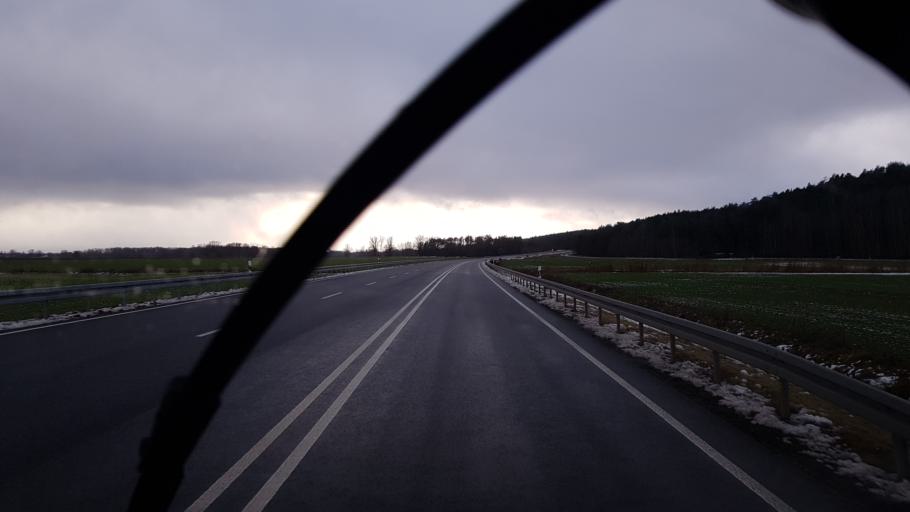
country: DE
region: Brandenburg
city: Schenkendobern
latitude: 51.8634
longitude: 14.6151
